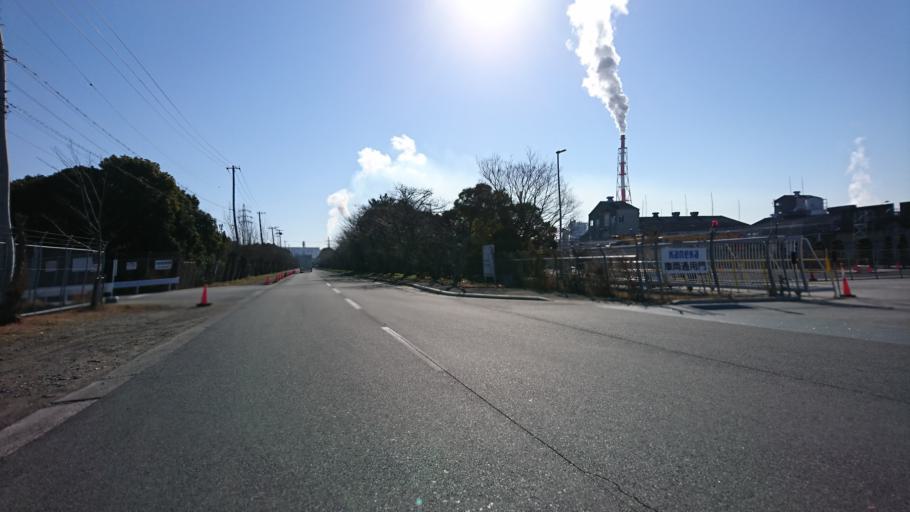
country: JP
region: Hyogo
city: Kakogawacho-honmachi
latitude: 34.7449
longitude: 134.7932
